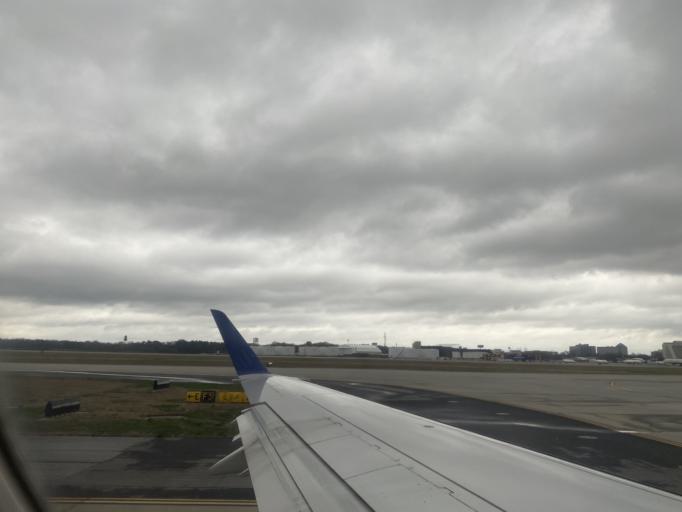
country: US
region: Georgia
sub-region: Fulton County
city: College Park
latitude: 33.6446
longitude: -84.4345
